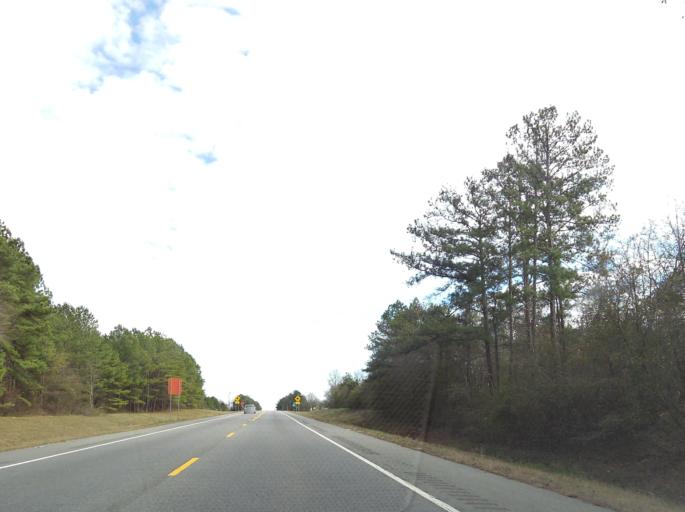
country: US
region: Georgia
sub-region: Bibb County
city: West Point
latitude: 32.7988
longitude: -83.7852
